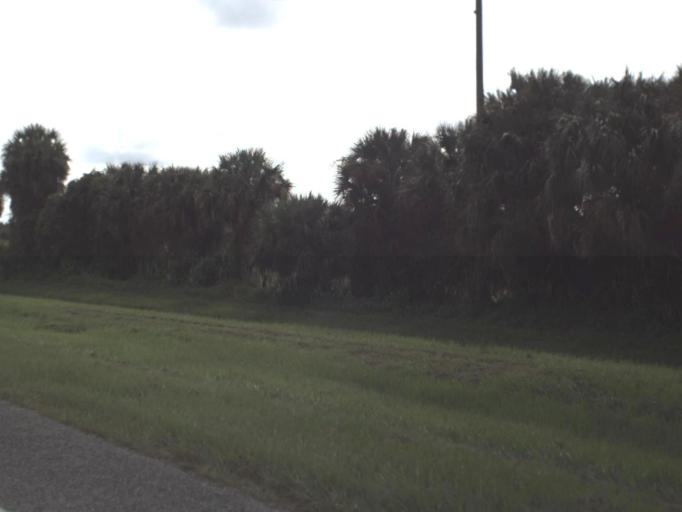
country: US
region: Florida
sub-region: Lee County
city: Alva
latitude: 26.7092
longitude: -81.5768
